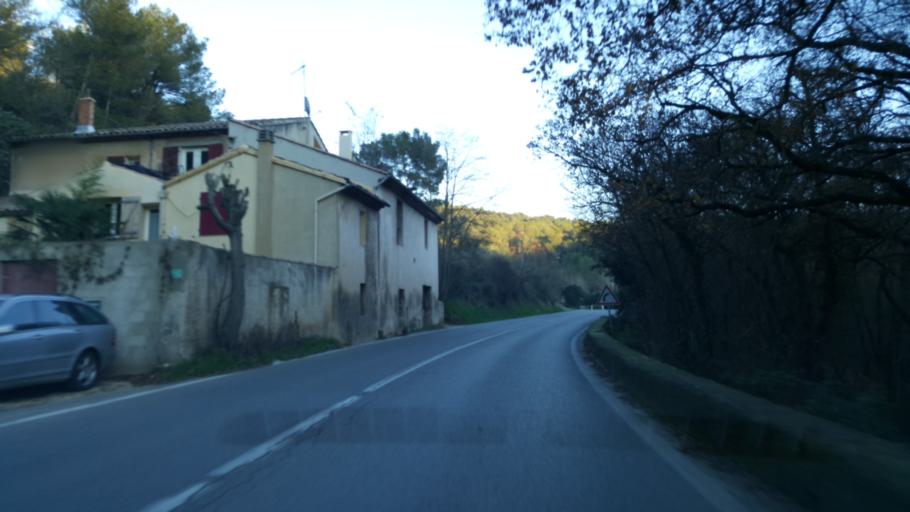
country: FR
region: Provence-Alpes-Cote d'Azur
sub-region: Departement des Bouches-du-Rhone
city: Le Tholonet
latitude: 43.5100
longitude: 5.5046
